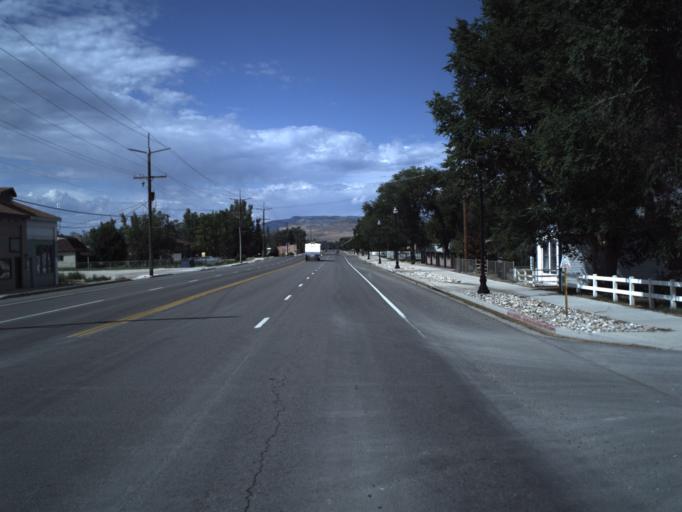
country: US
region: Utah
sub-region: Sanpete County
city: Centerfield
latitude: 39.1247
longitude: -111.8192
